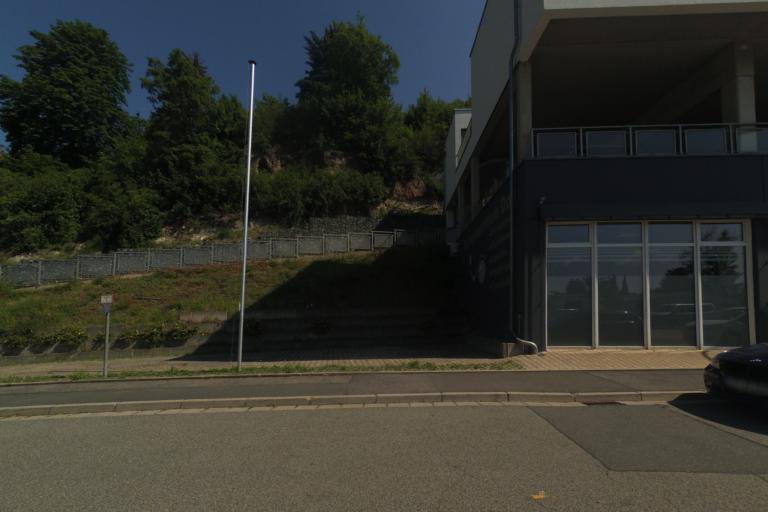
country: DE
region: Bavaria
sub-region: Upper Franconia
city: Burgkunstadt
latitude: 50.1438
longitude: 11.2403
